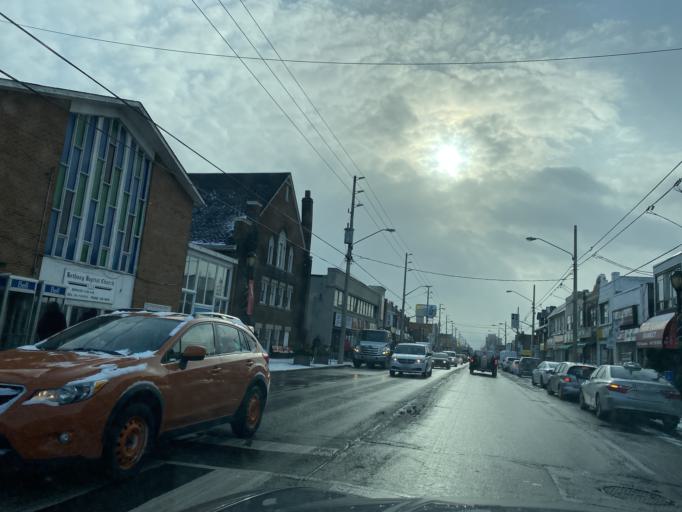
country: CA
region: Ontario
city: Toronto
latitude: 43.6894
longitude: -79.3489
